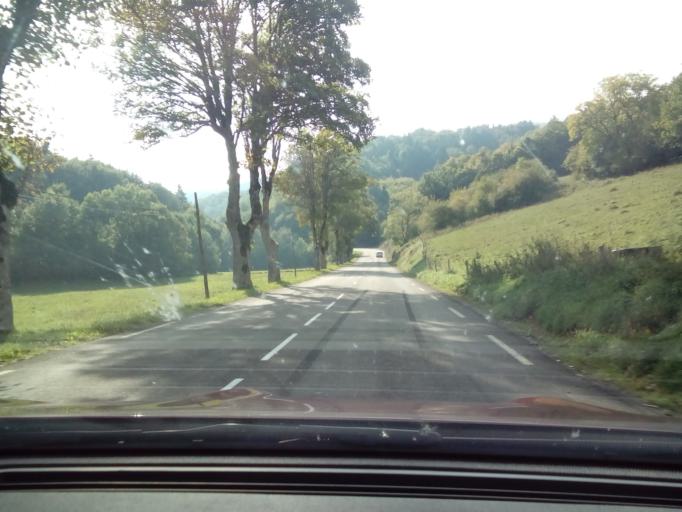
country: FR
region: Rhone-Alpes
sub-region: Departement de la Drome
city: Saint-Laurent-en-Royans
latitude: 44.9930
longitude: 5.4158
